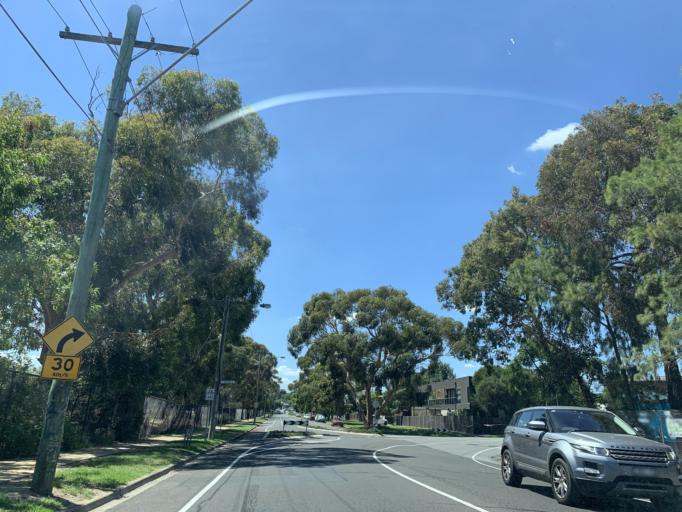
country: AU
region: Victoria
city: Ripponlea
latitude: -37.8880
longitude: 144.9962
